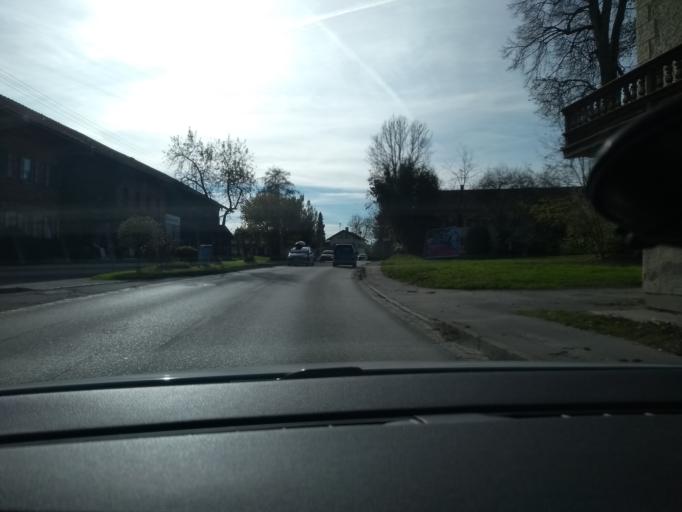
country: DE
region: Bavaria
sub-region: Upper Bavaria
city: Prutting
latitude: 47.8868
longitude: 12.1897
